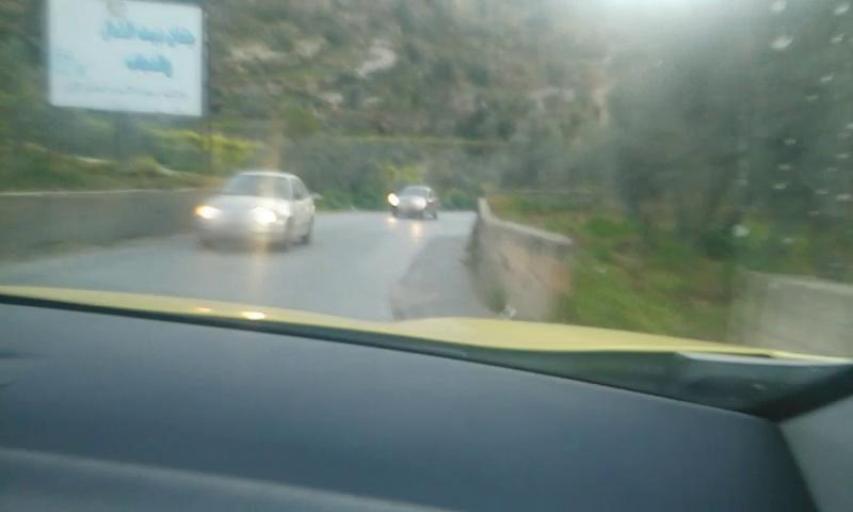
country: PS
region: West Bank
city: `Ayn Yabrud
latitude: 31.9517
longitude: 35.2409
